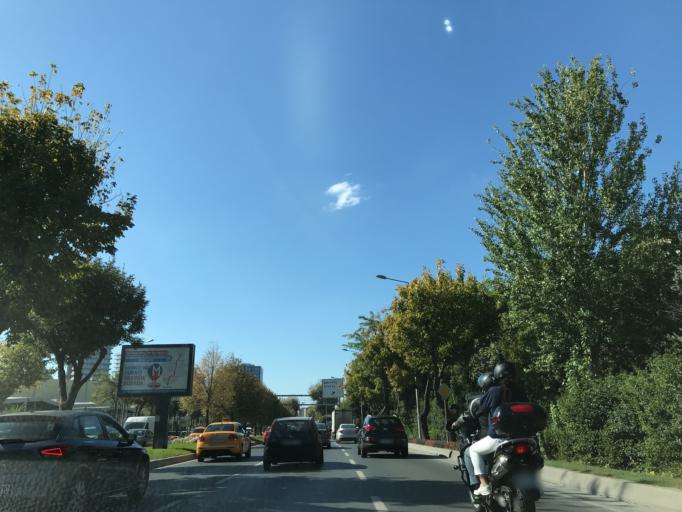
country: TR
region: Istanbul
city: Bahcelievler
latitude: 40.9752
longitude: 28.8703
